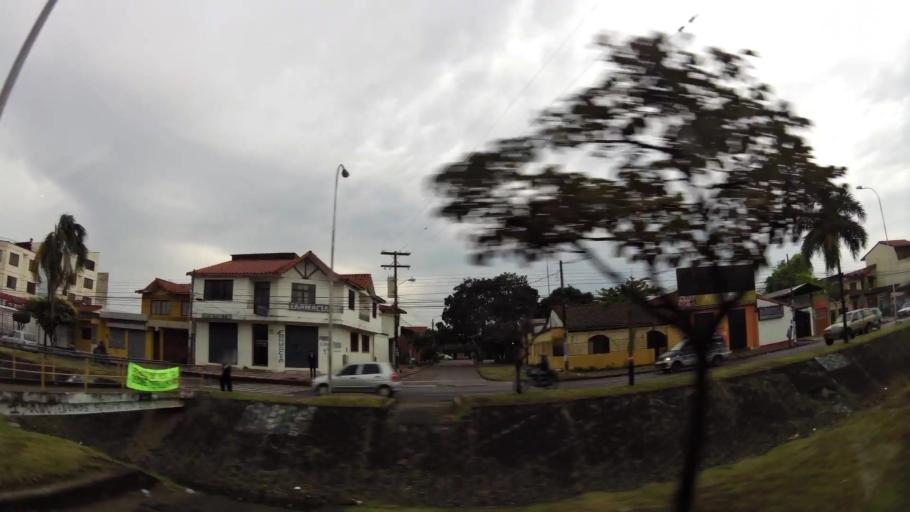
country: BO
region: Santa Cruz
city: Santa Cruz de la Sierra
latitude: -17.7819
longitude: -63.1602
